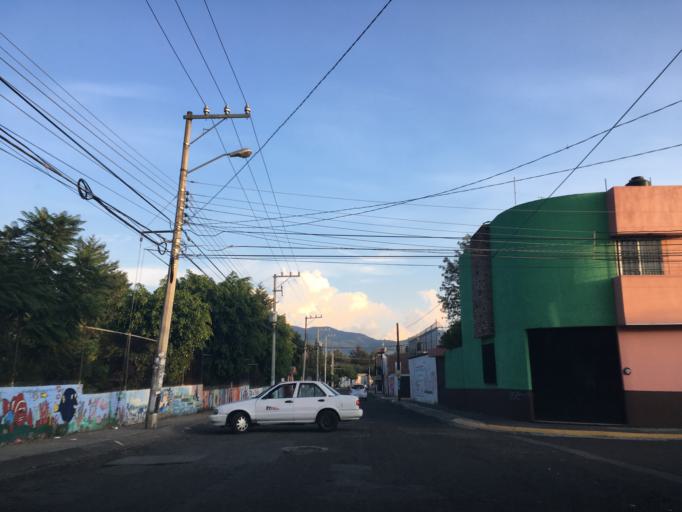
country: MX
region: Michoacan
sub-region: Morelia
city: Morelos
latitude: 19.6866
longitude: -101.2300
